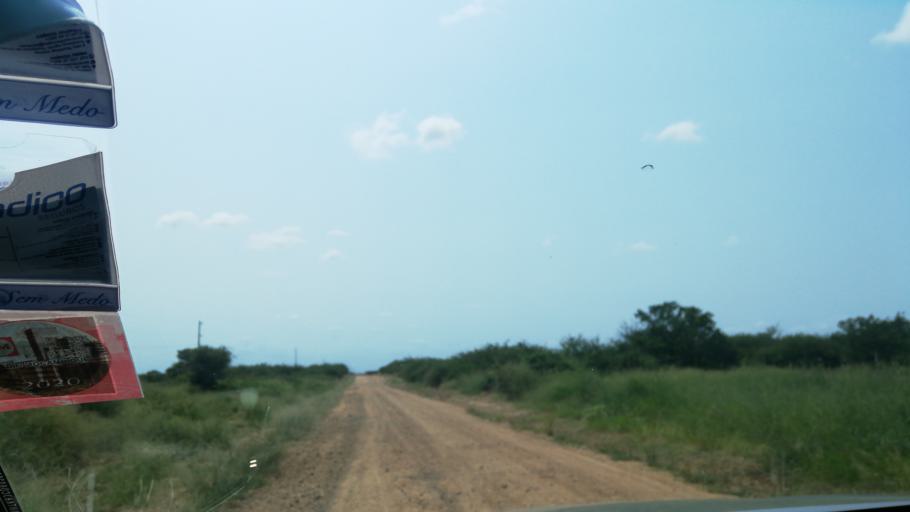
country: MZ
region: Maputo
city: Matola
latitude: -26.0800
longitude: 32.3912
